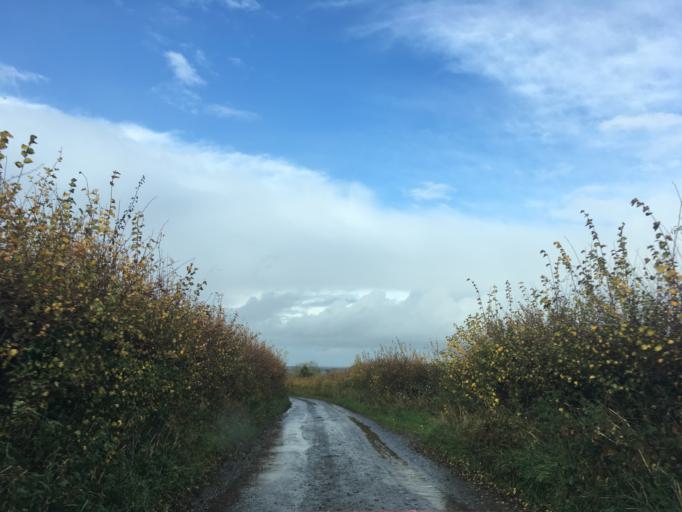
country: GB
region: England
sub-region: South Gloucestershire
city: Hinton
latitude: 51.4565
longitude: -2.4060
